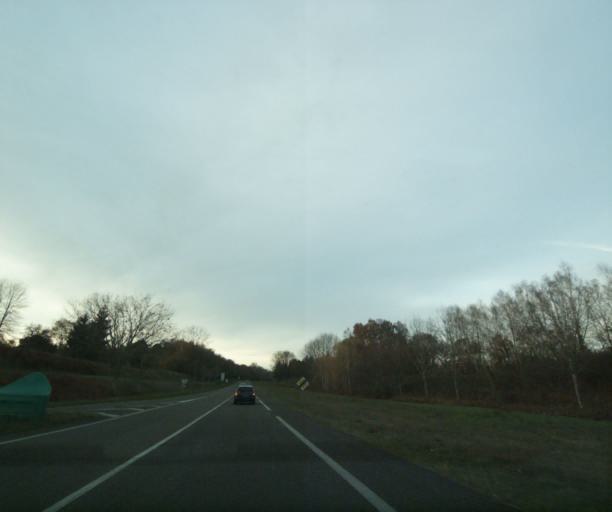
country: FR
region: Aquitaine
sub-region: Departement de la Gironde
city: Bazas
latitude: 44.4294
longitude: -0.2326
